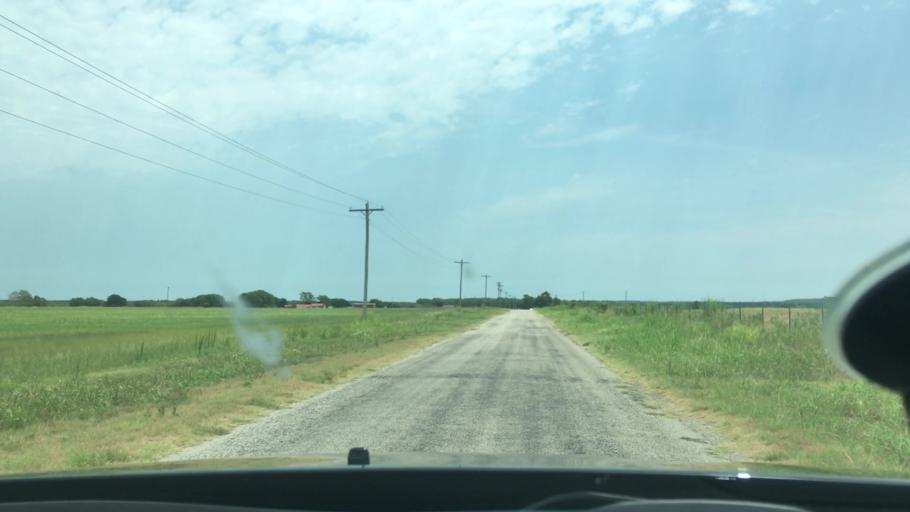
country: US
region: Texas
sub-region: Cooke County
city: Muenster
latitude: 33.8676
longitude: -97.3643
